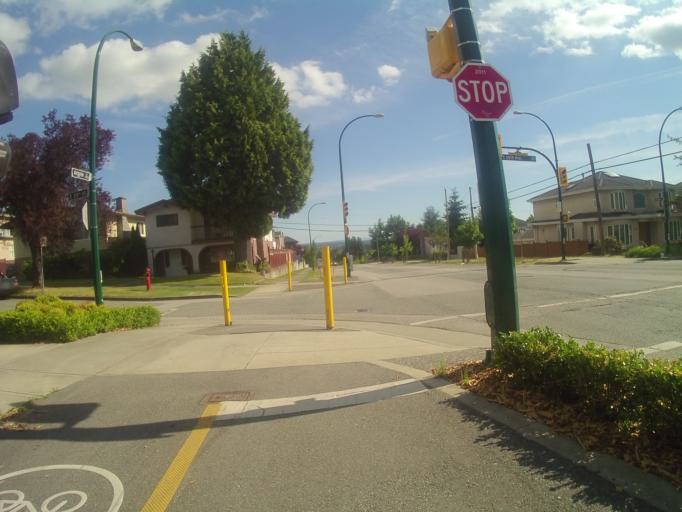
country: CA
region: British Columbia
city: Vancouver
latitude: 49.2164
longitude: -123.0719
